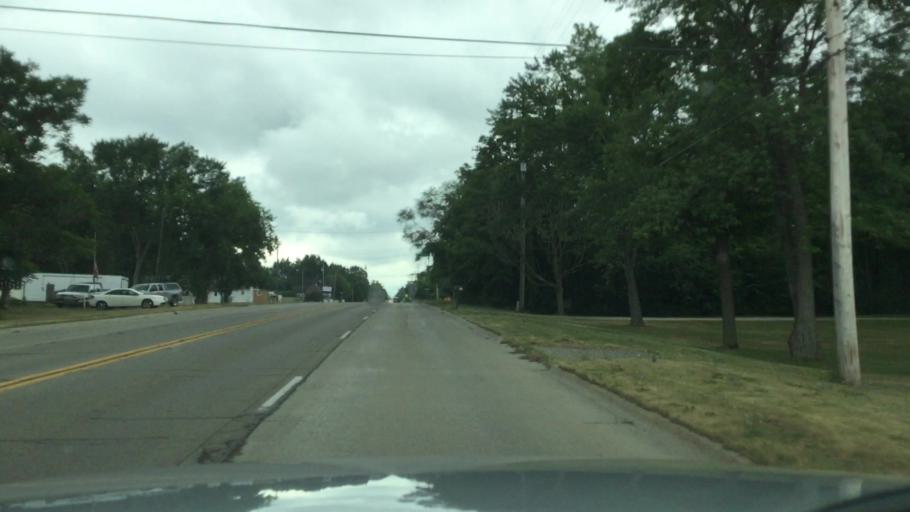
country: US
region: Michigan
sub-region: Genesee County
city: Burton
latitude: 43.0779
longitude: -83.6169
